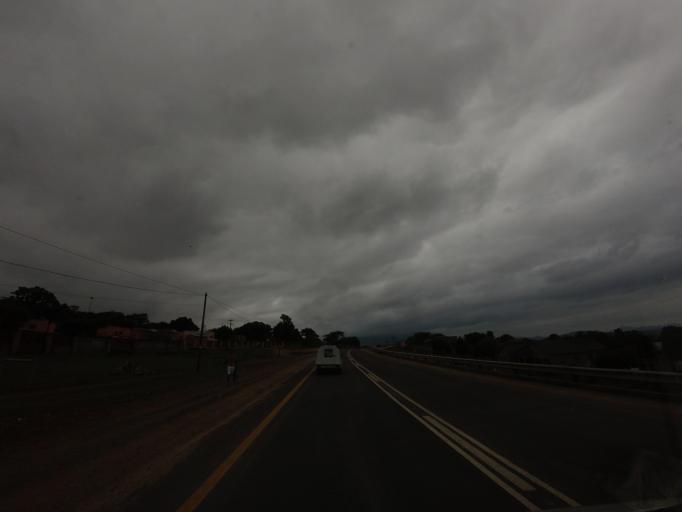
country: SZ
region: Hhohho
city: Ntfonjeni
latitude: -25.6883
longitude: 31.4966
